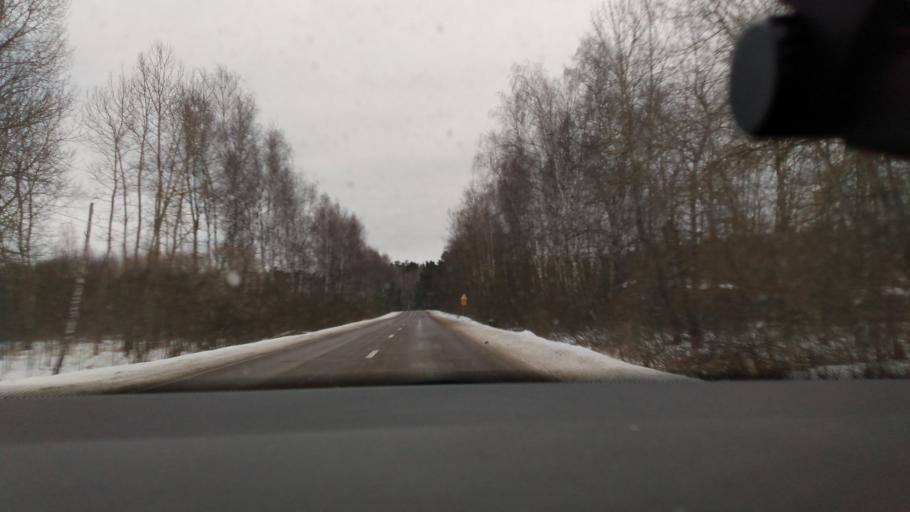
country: RU
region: Moskovskaya
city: Yegor'yevsk
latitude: 55.2263
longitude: 39.0704
